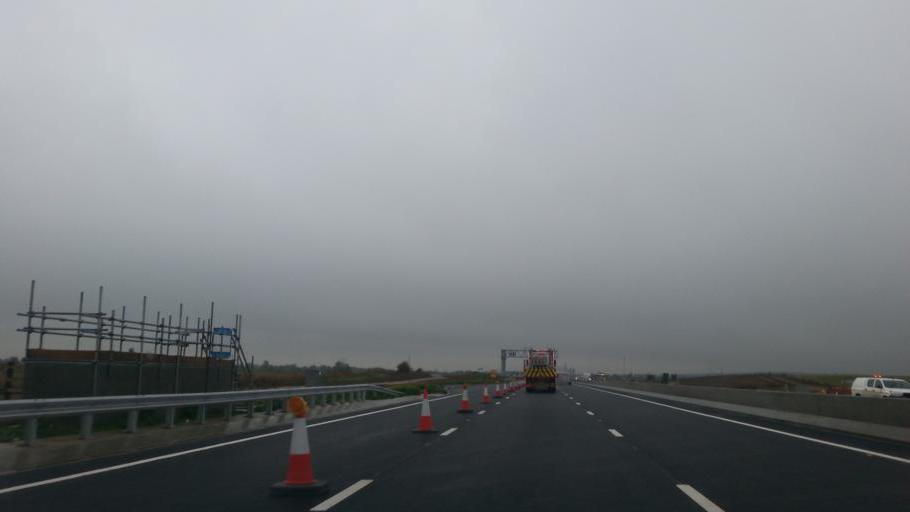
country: GB
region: England
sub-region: Cambridgeshire
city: Great Stukeley
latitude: 52.3495
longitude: -0.2515
